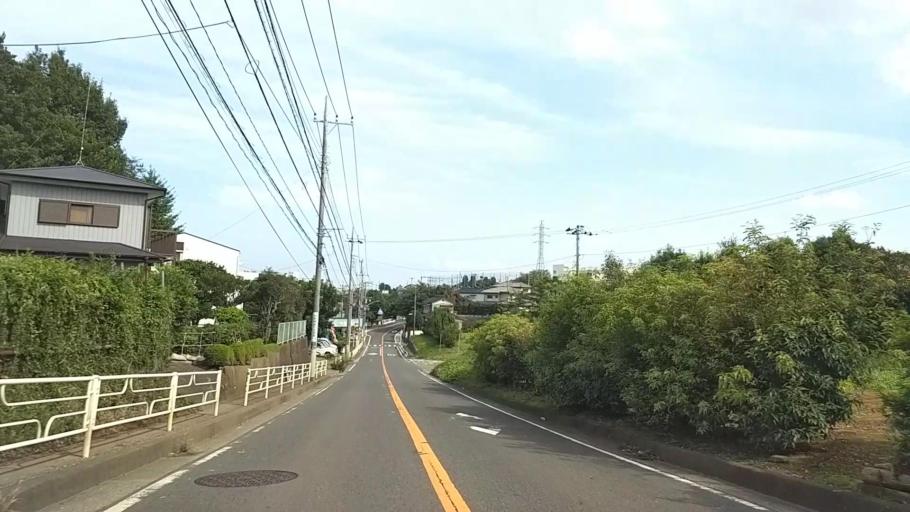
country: JP
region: Kanagawa
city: Yokohama
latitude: 35.4958
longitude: 139.5850
